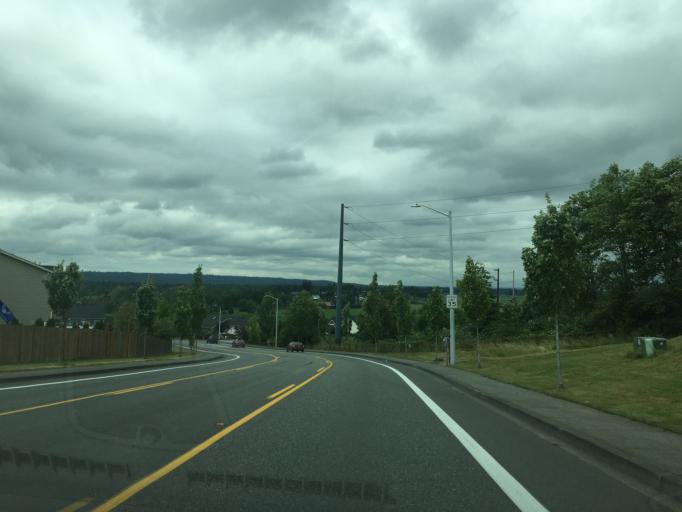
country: US
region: Washington
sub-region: Snohomish County
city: Sisco Heights
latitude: 48.0763
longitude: -122.1251
